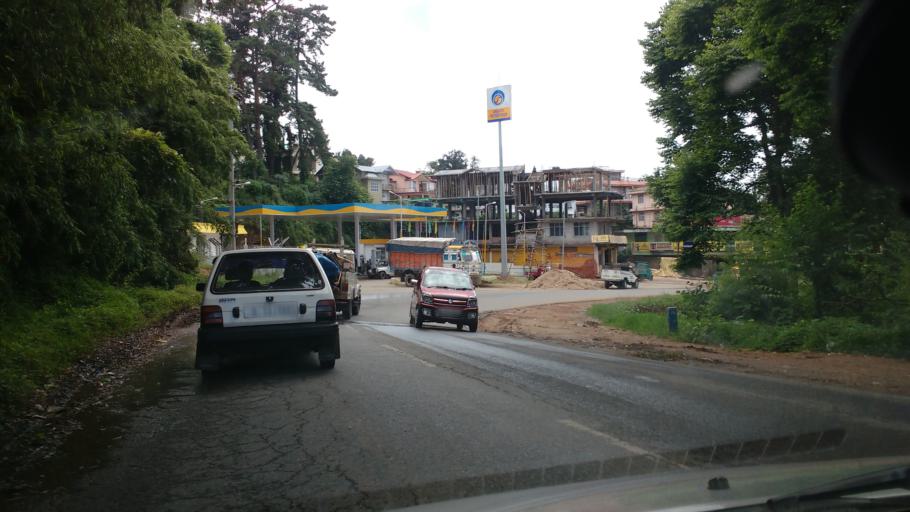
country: IN
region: Meghalaya
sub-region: East Khasi Hills
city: Shillong
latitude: 25.5624
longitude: 91.8543
